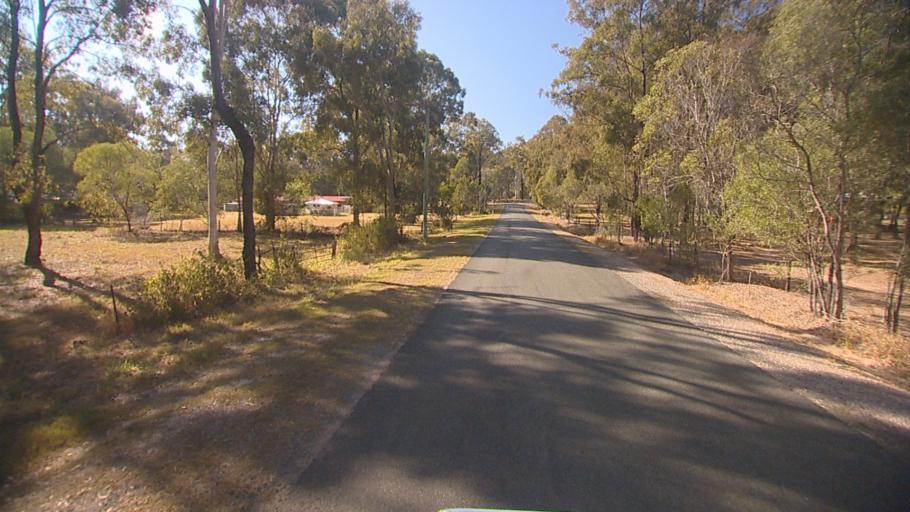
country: AU
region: Queensland
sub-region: Logan
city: Chambers Flat
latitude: -27.7874
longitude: 153.1340
